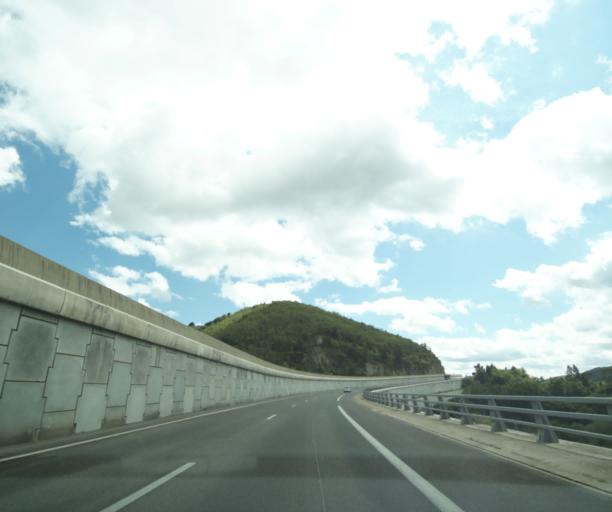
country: FR
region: Languedoc-Roussillon
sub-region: Departement de l'Herault
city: Lodeve
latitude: 43.7410
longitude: 3.3305
